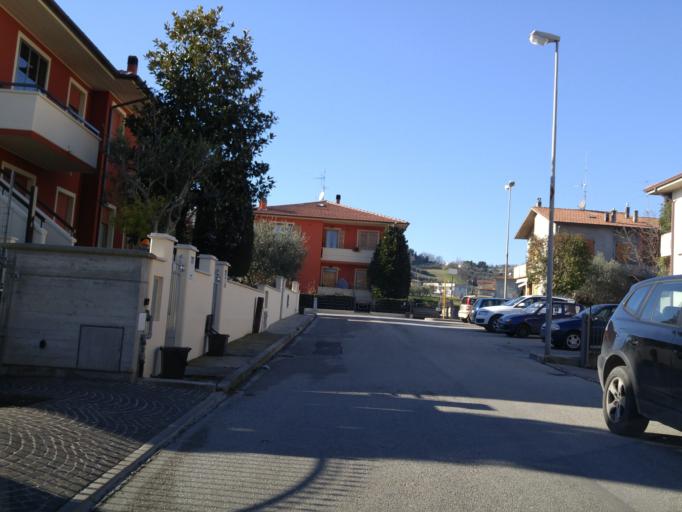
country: IT
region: The Marches
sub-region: Provincia di Pesaro e Urbino
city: Calcinelli
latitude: 43.7553
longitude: 12.9125
